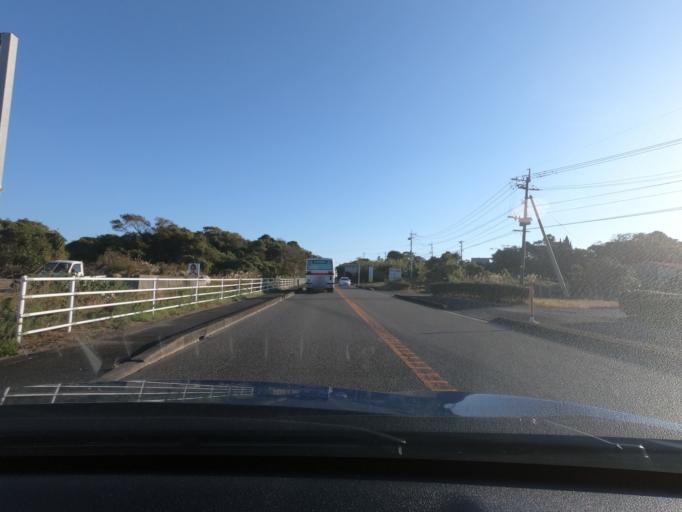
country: JP
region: Kagoshima
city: Akune
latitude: 31.9796
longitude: 130.2036
